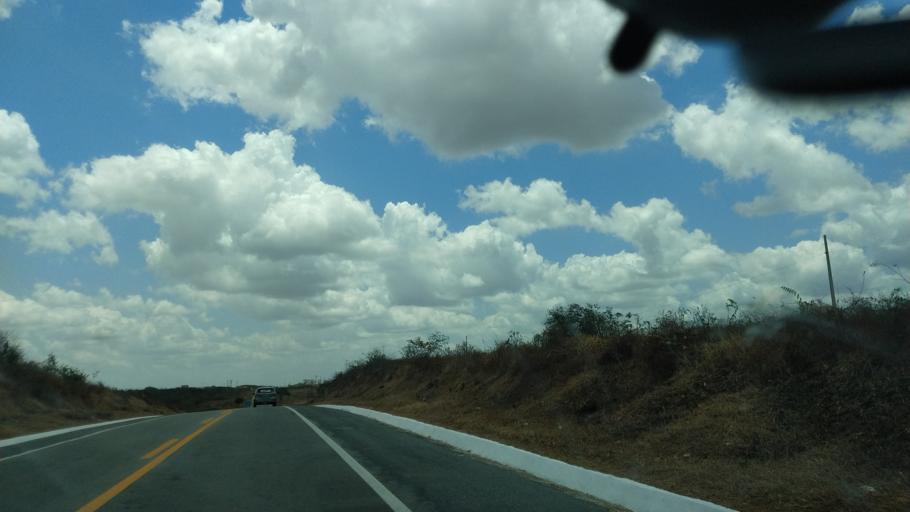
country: BR
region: Rio Grande do Norte
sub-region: Cerro Cora
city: Cerro Cora
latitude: -6.1898
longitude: -36.2275
